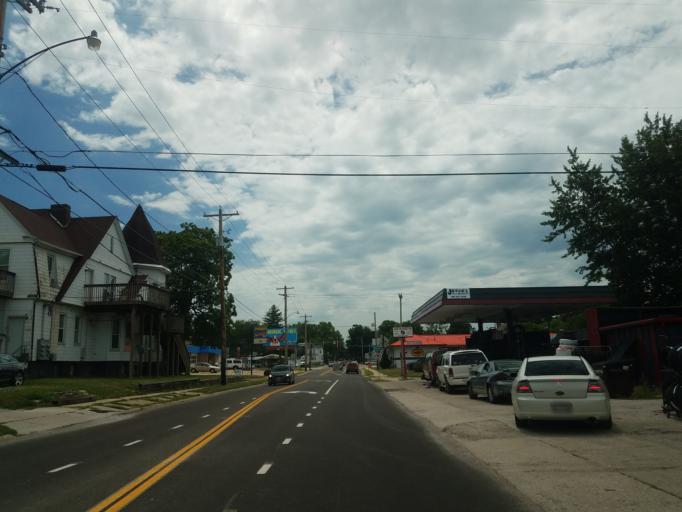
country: US
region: Illinois
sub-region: McLean County
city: Bloomington
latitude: 40.4811
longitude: -88.9847
